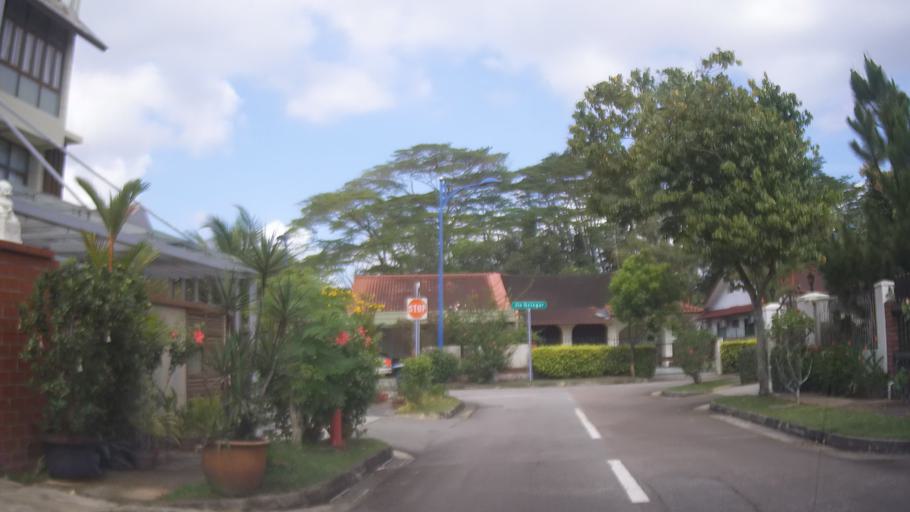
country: MY
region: Johor
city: Johor Bahru
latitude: 1.4161
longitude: 103.7581
